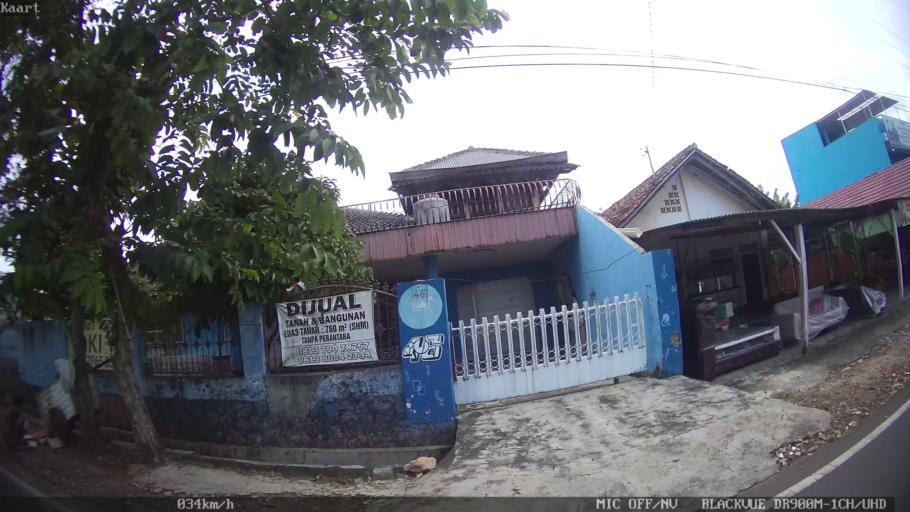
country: ID
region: Lampung
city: Kedaton
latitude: -5.4028
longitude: 105.2429
